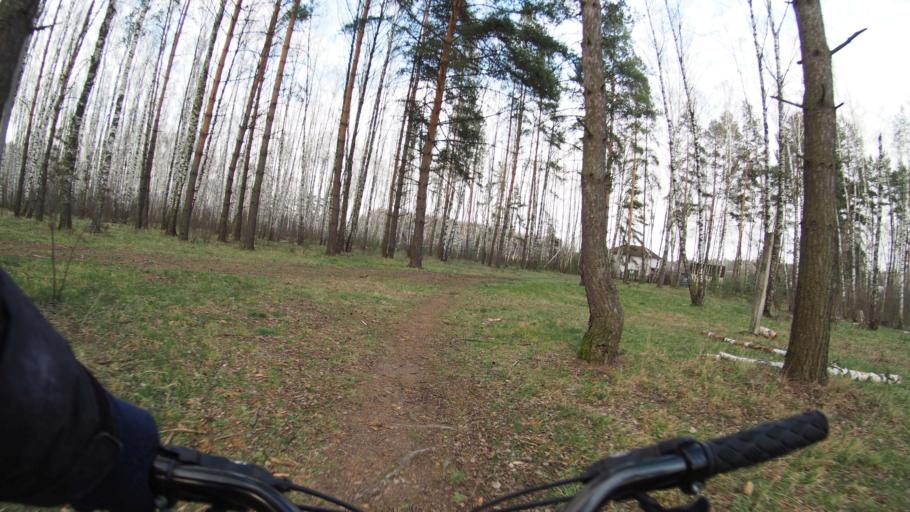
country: RU
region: Moskovskaya
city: Malyshevo
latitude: 55.5189
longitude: 38.3060
